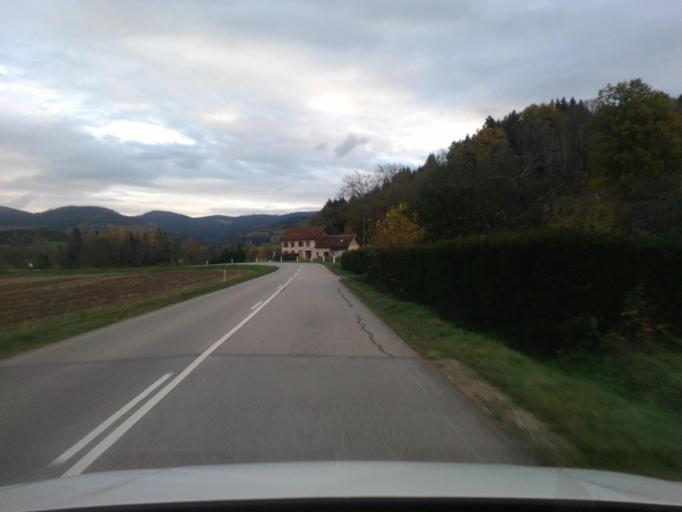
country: FR
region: Lorraine
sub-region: Departement des Vosges
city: Ban-de-Laveline
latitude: 48.2550
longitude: 7.0566
